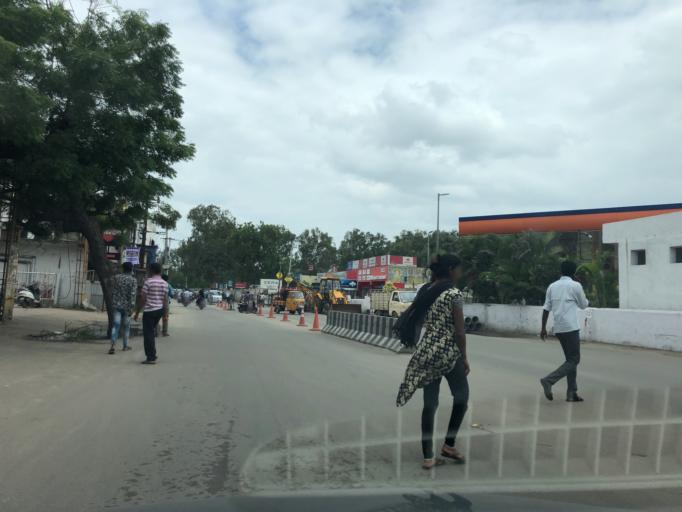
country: IN
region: Telangana
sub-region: Rangareddi
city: Quthbullapur
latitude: 17.4687
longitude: 78.4811
